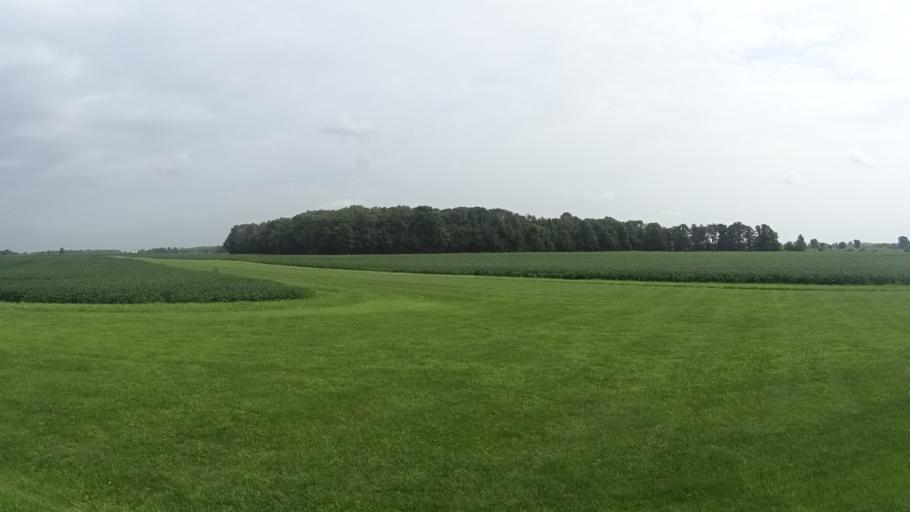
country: US
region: Indiana
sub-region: Madison County
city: Pendleton
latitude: 40.0282
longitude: -85.7837
